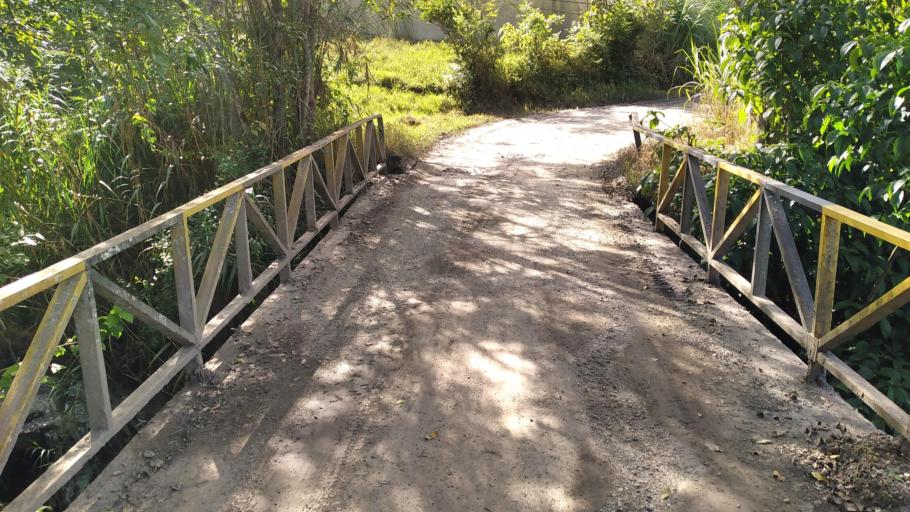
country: CO
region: Cundinamarca
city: Tenza
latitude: 5.0700
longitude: -73.4176
